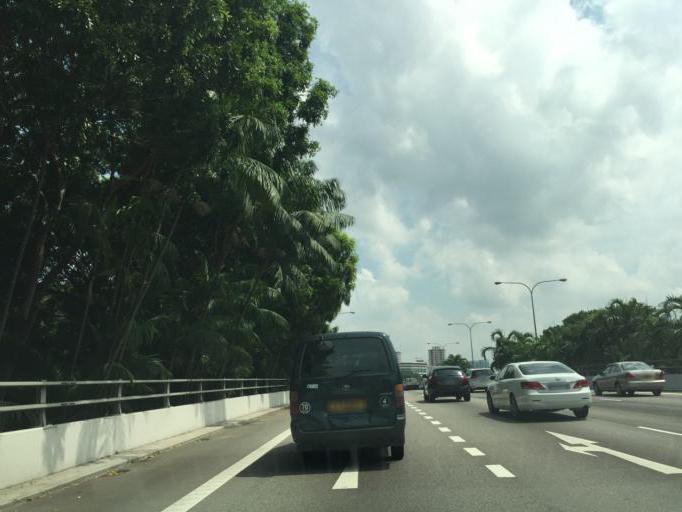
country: SG
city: Singapore
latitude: 1.3211
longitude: 103.8826
